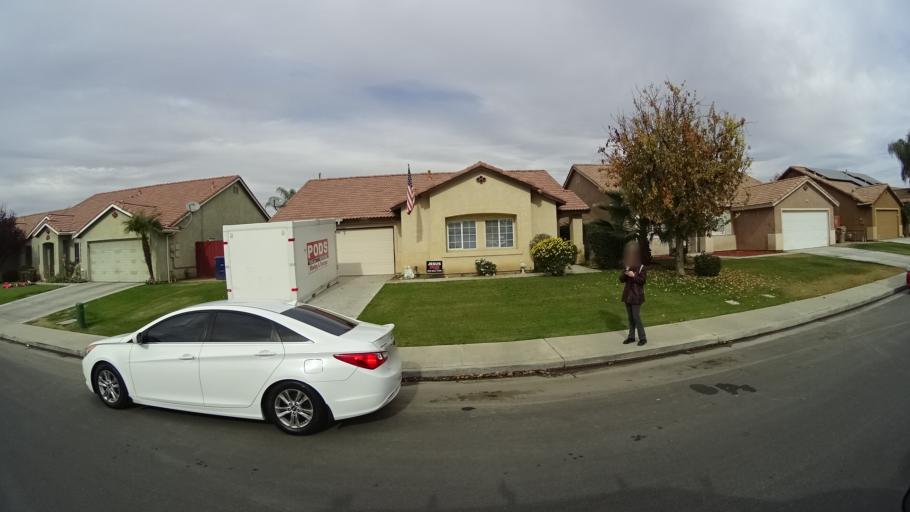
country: US
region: California
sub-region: Kern County
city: Rosedale
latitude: 35.4229
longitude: -119.1344
